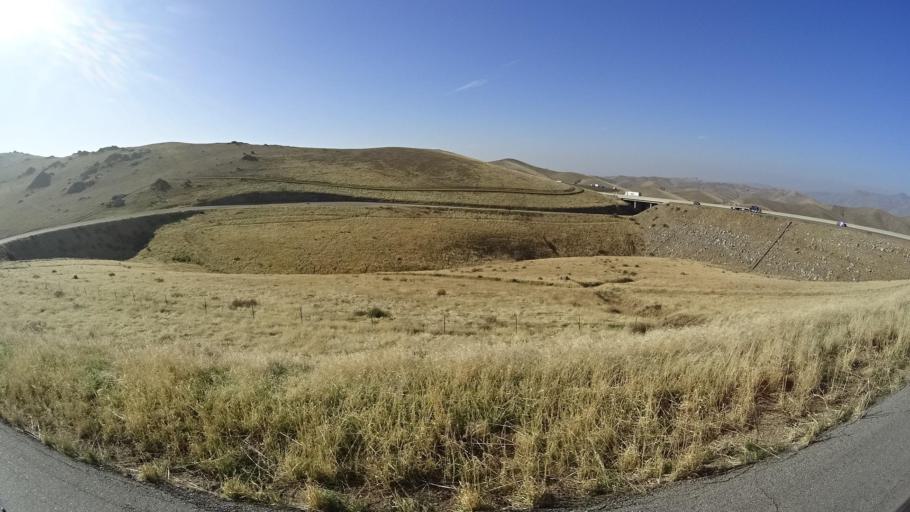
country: US
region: California
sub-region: Kern County
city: Bear Valley Springs
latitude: 35.2682
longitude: -118.6798
